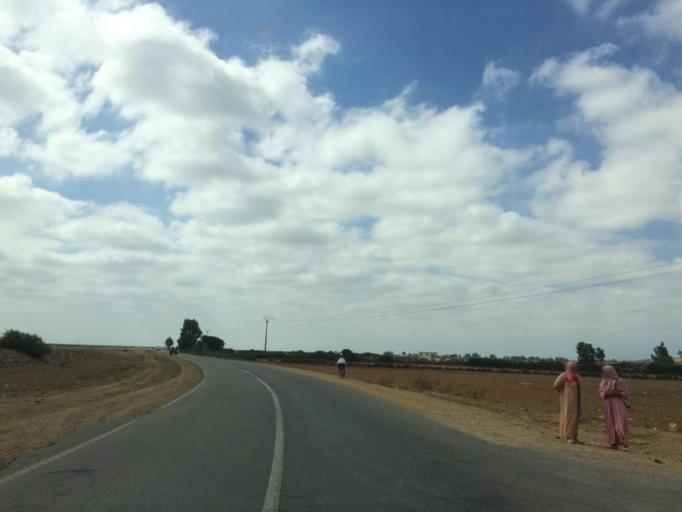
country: MA
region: Gharb-Chrarda-Beni Hssen
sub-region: Kenitra Province
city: Lalla Mimouna
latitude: 34.7699
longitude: -6.0928
